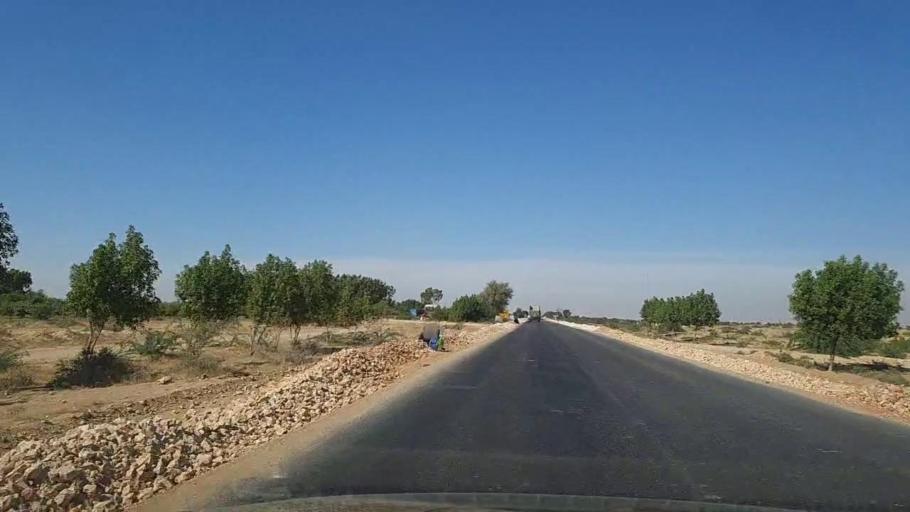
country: PK
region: Sindh
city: Kotri
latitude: 25.2621
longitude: 68.2218
